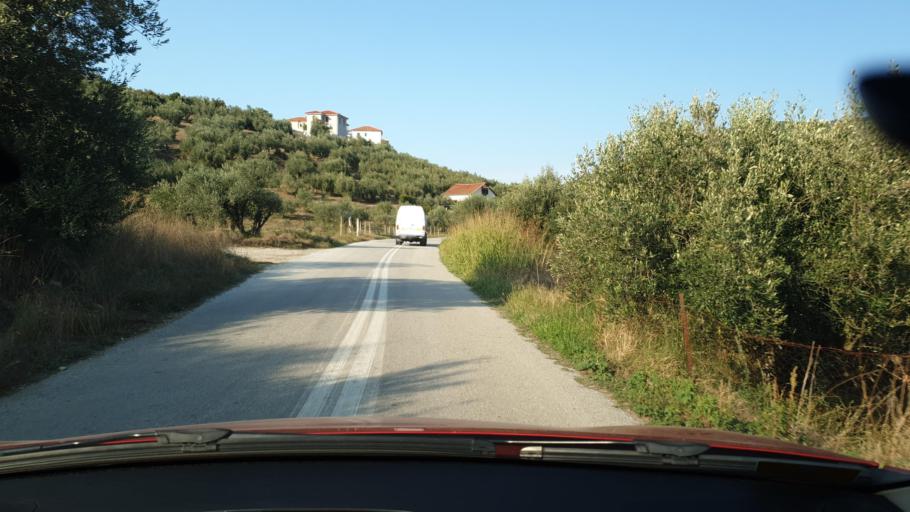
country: GR
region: Thessaly
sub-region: Nomos Magnisias
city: Pteleos
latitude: 39.0000
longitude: 22.9620
